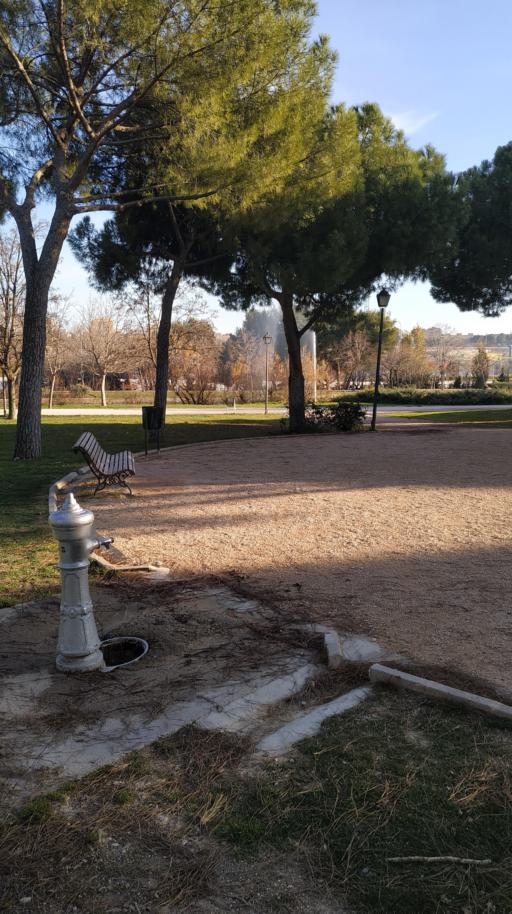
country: ES
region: Madrid
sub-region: Provincia de Madrid
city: Arganzuela
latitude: 40.3892
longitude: -3.6814
